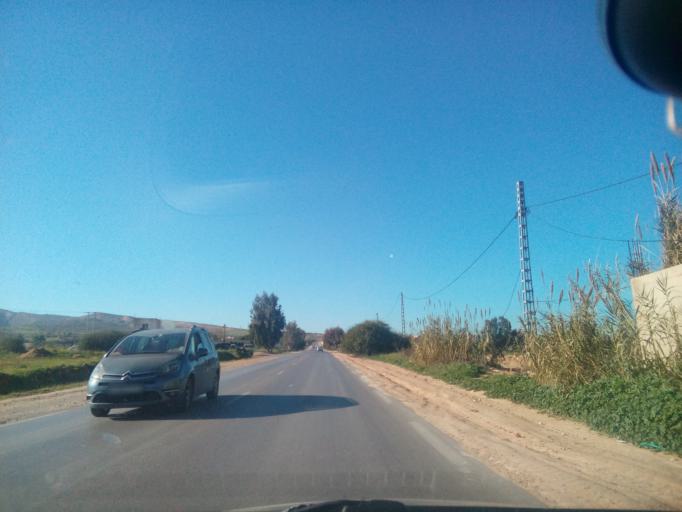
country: DZ
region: Relizane
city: Relizane
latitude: 35.9023
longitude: 0.5238
